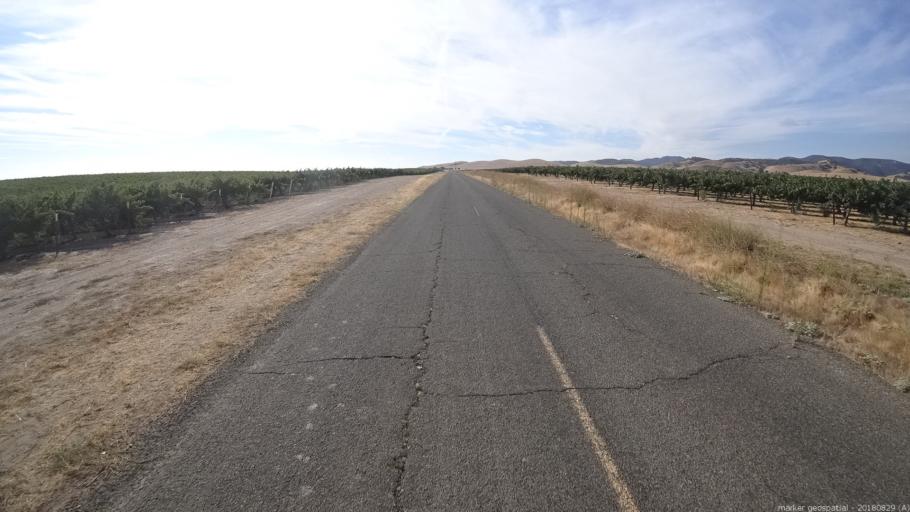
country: US
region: California
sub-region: Monterey County
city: King City
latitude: 36.0634
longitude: -120.9847
